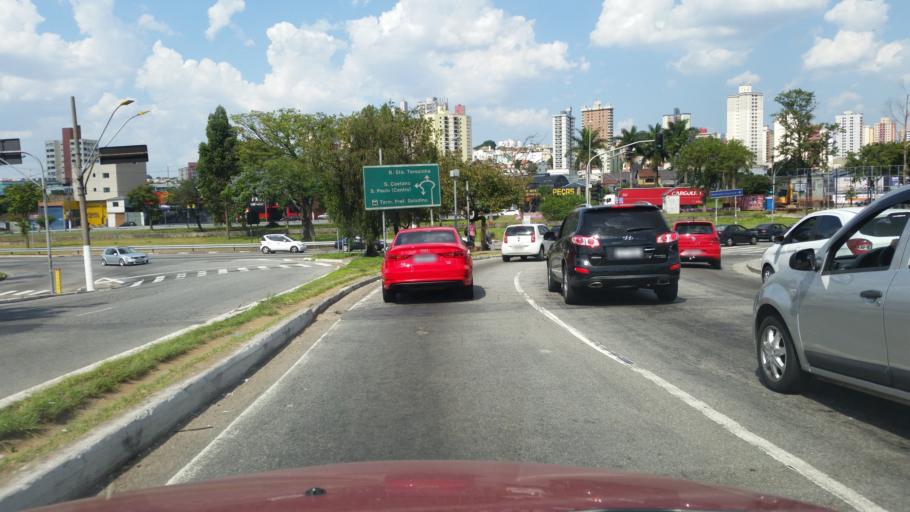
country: BR
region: Sao Paulo
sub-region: Sao Caetano Do Sul
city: Sao Caetano do Sul
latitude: -23.6384
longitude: -46.5355
